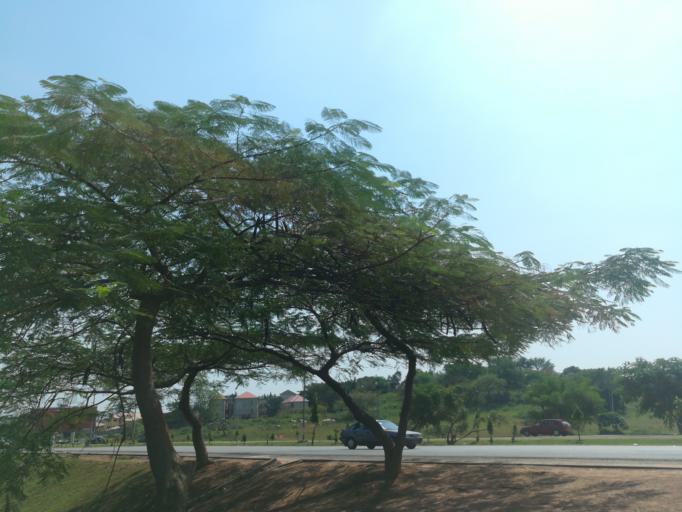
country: NG
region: Abuja Federal Capital Territory
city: Abuja
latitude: 9.0774
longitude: 7.4579
